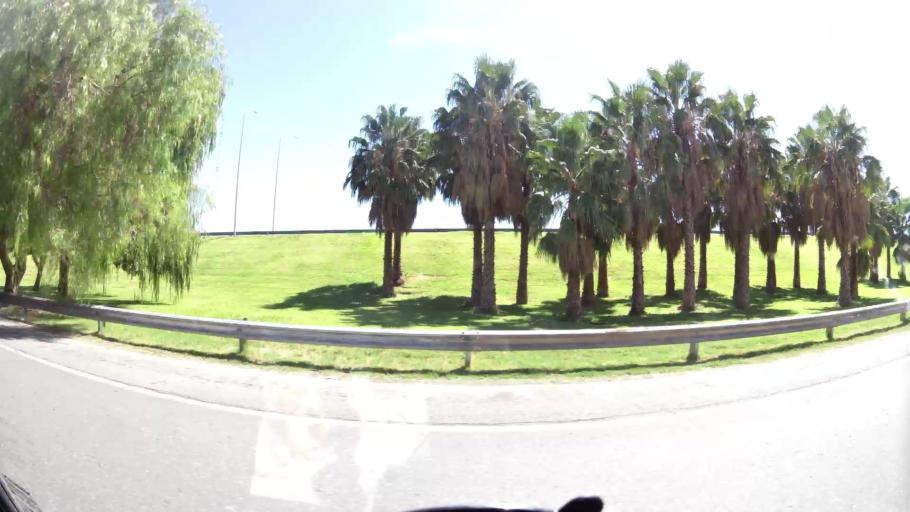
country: AR
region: San Juan
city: San Juan
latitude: -31.5227
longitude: -68.5399
